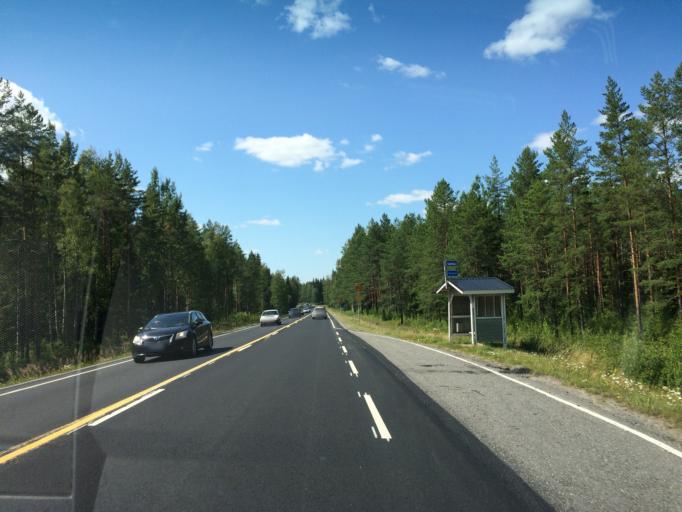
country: FI
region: Pirkanmaa
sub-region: Lounais-Pirkanmaa
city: Kiikoinen
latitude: 61.4754
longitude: 22.4669
